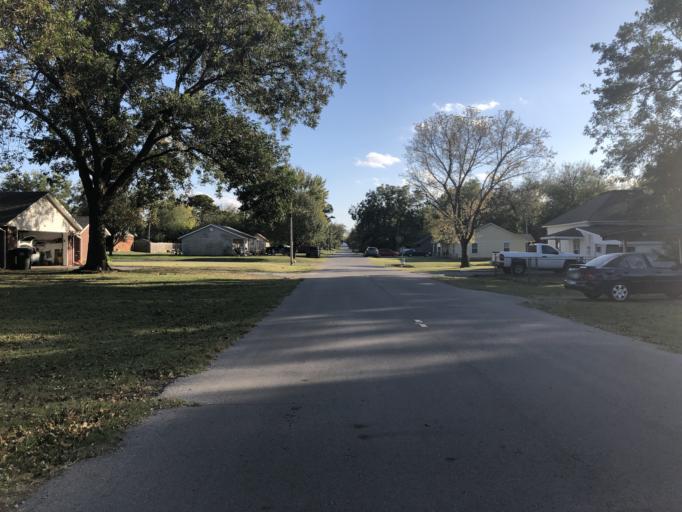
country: US
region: Oklahoma
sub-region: Pottawatomie County
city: Tecumseh
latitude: 35.2582
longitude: -96.9317
